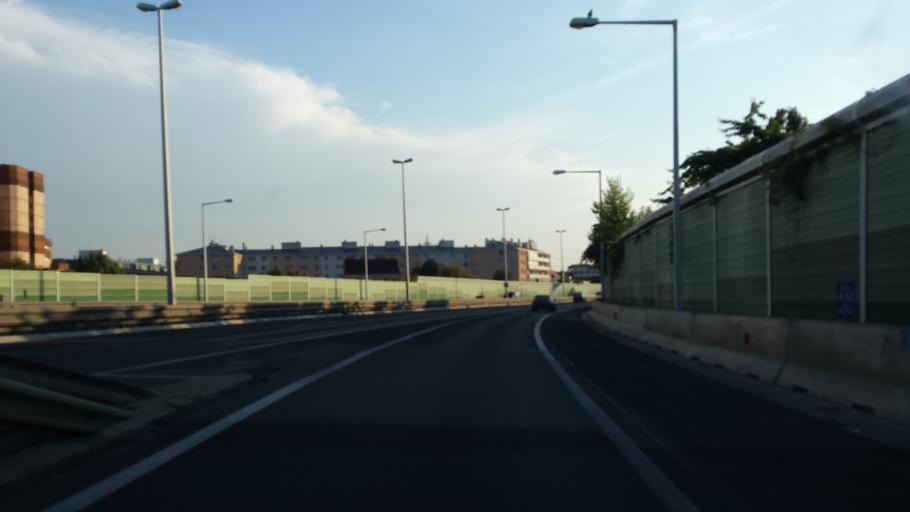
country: AT
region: Vienna
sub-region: Wien Stadt
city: Vienna
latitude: 48.2607
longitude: 16.3932
